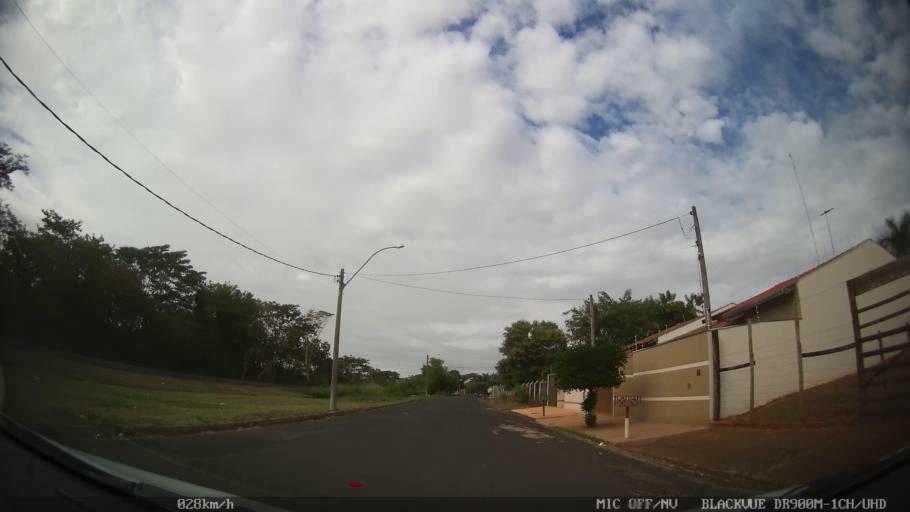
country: BR
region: Sao Paulo
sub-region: Sao Jose Do Rio Preto
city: Sao Jose do Rio Preto
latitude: -20.8183
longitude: -49.3498
